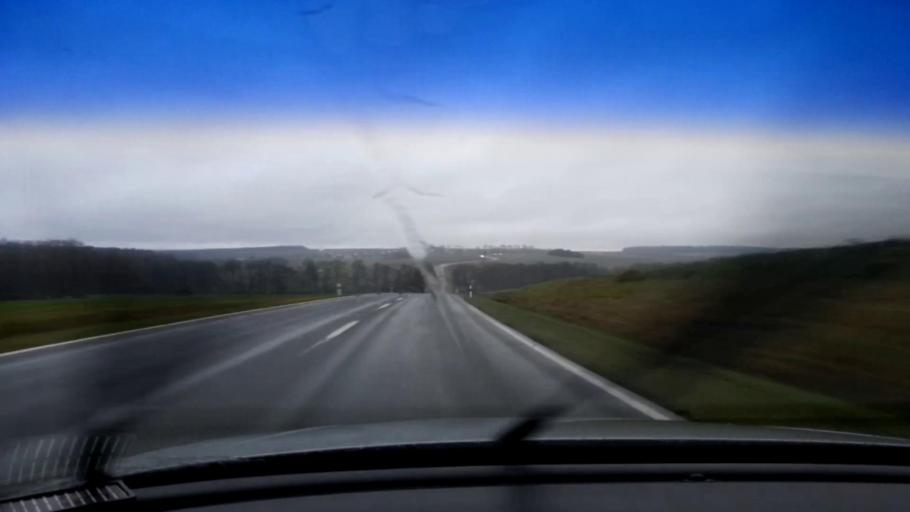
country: DE
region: Bavaria
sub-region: Upper Franconia
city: Schesslitz
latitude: 49.9852
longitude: 11.0152
